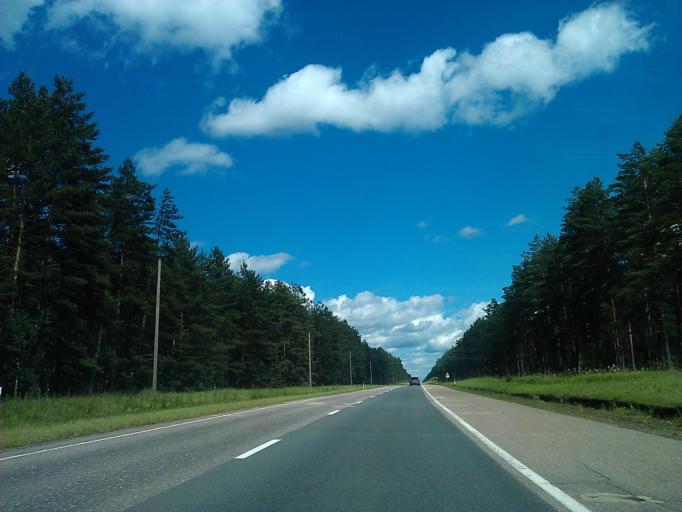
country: LV
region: Garkalne
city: Garkalne
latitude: 57.0593
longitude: 24.4603
